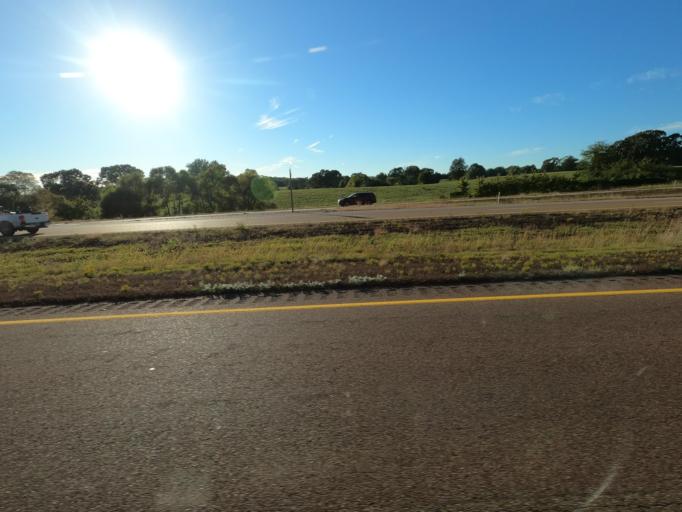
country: US
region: Tennessee
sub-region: Fayette County
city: Hickory Withe
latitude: 35.1532
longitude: -89.6381
